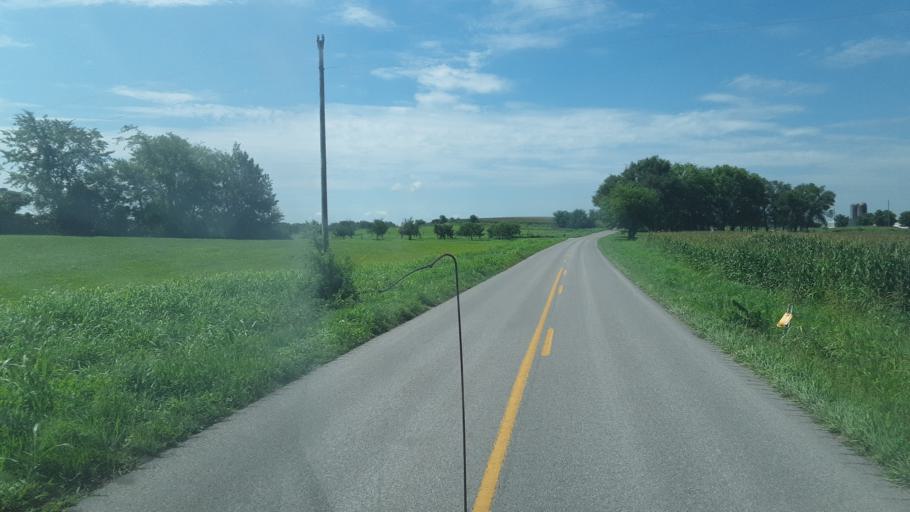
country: US
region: Kentucky
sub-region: Todd County
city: Elkton
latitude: 36.8088
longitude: -87.3147
